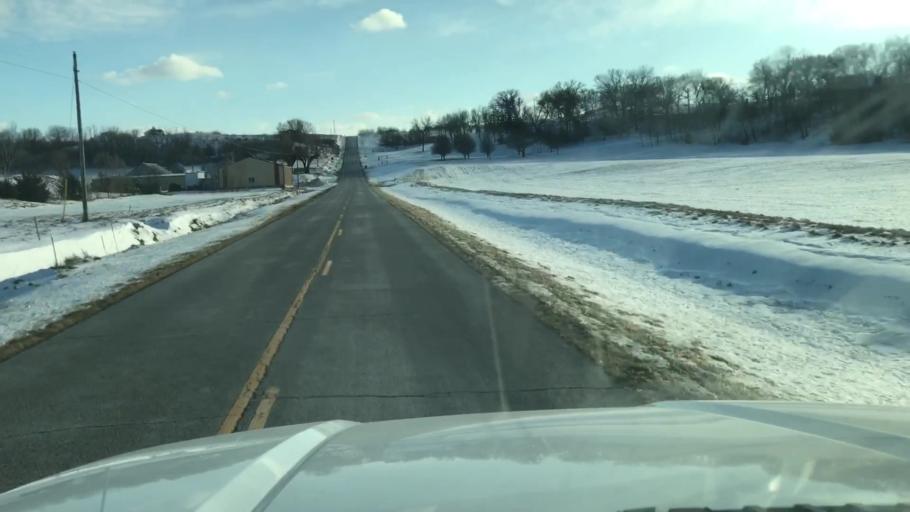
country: US
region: Missouri
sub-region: Holt County
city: Oregon
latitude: 40.0741
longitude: -94.9747
